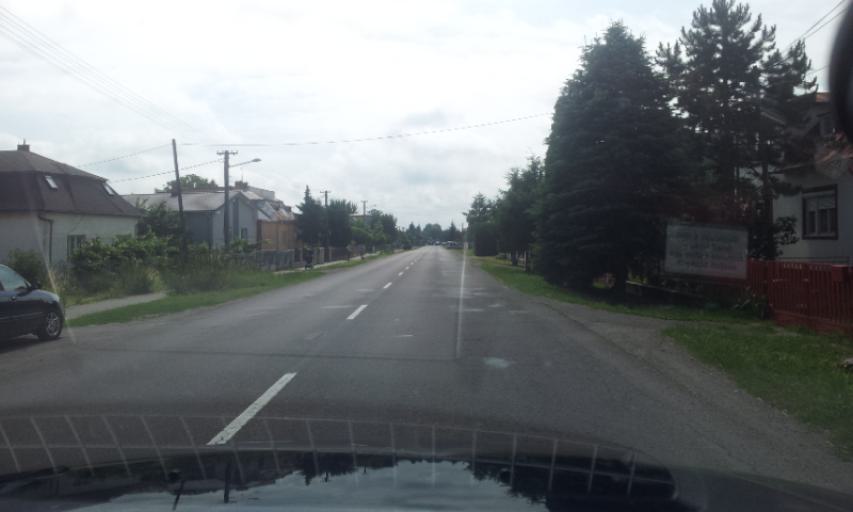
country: SK
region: Kosicky
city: Michalovce
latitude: 48.7403
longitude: 21.9448
